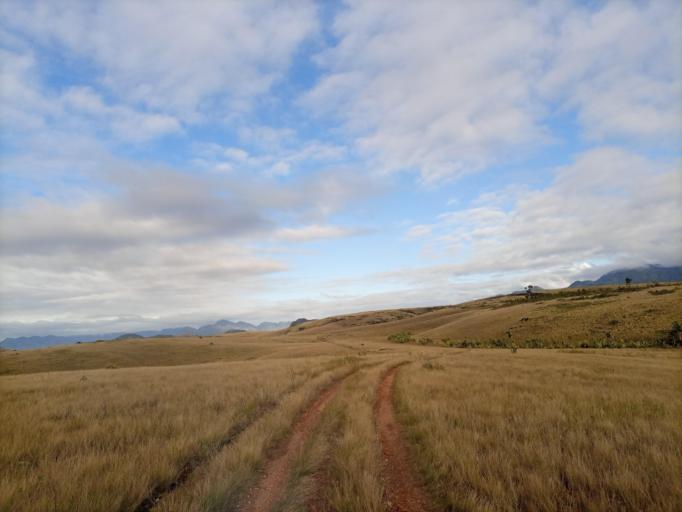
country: MG
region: Anosy
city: Fort Dauphin
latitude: -24.3113
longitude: 47.2424
